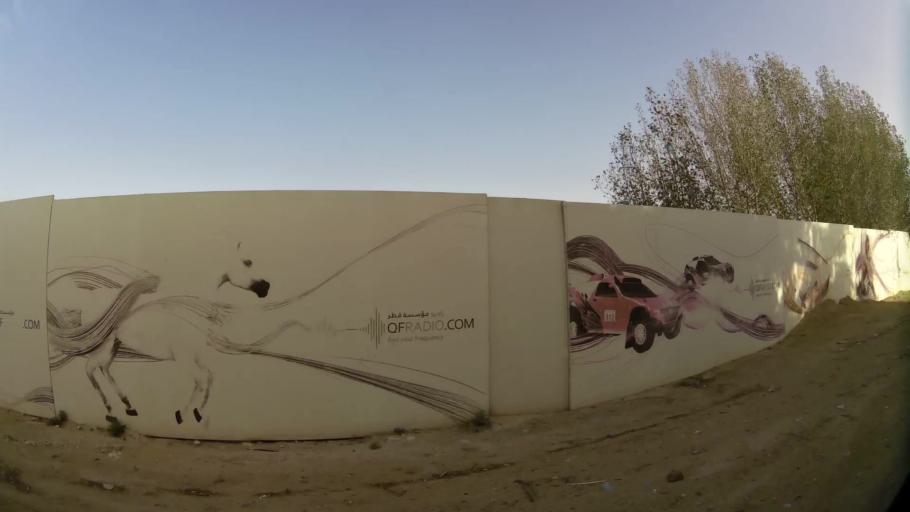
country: QA
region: Baladiyat ar Rayyan
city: Ar Rayyan
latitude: 25.3303
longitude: 51.4307
